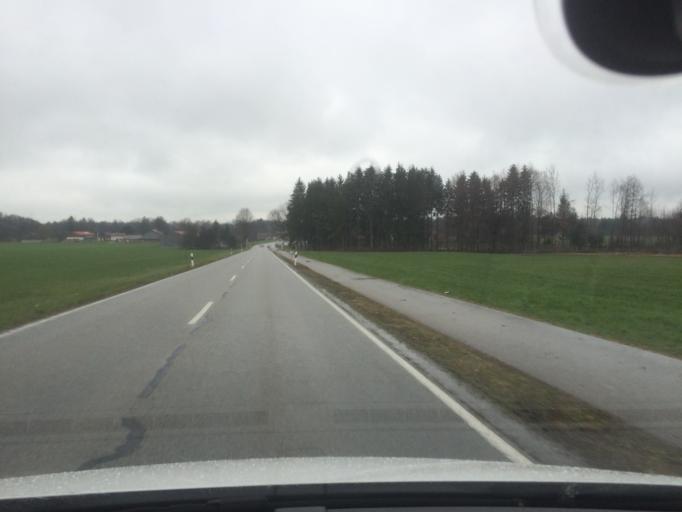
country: DE
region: Bavaria
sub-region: Upper Bavaria
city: Bad Aibling
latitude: 47.8864
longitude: 12.0359
